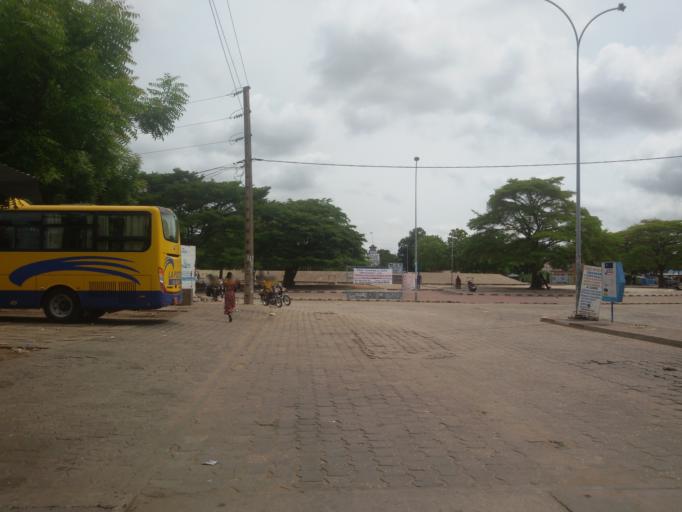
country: BJ
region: Littoral
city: Cotonou
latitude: 6.3690
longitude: 2.4467
